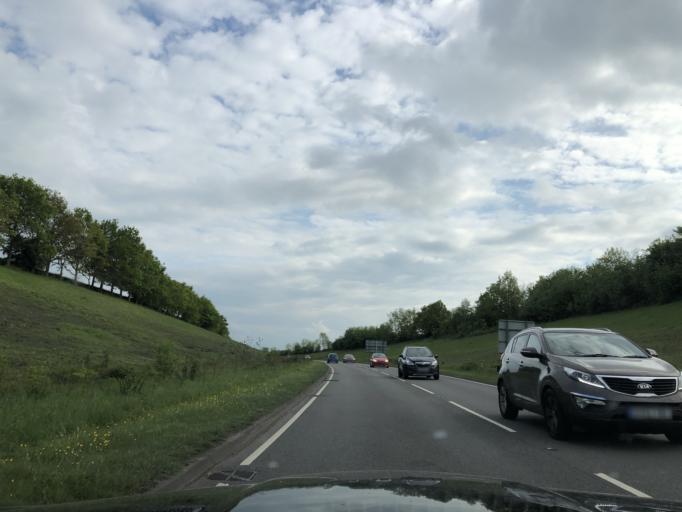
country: GB
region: England
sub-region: Warwickshire
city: Wellesbourne Mountford
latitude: 52.1406
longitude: -1.6150
